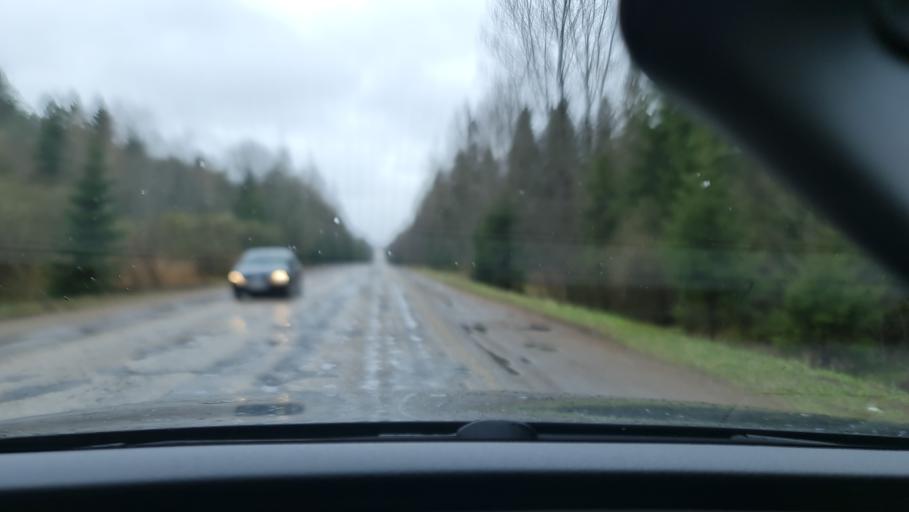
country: RU
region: Novgorod
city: Valday
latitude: 58.0355
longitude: 32.8688
